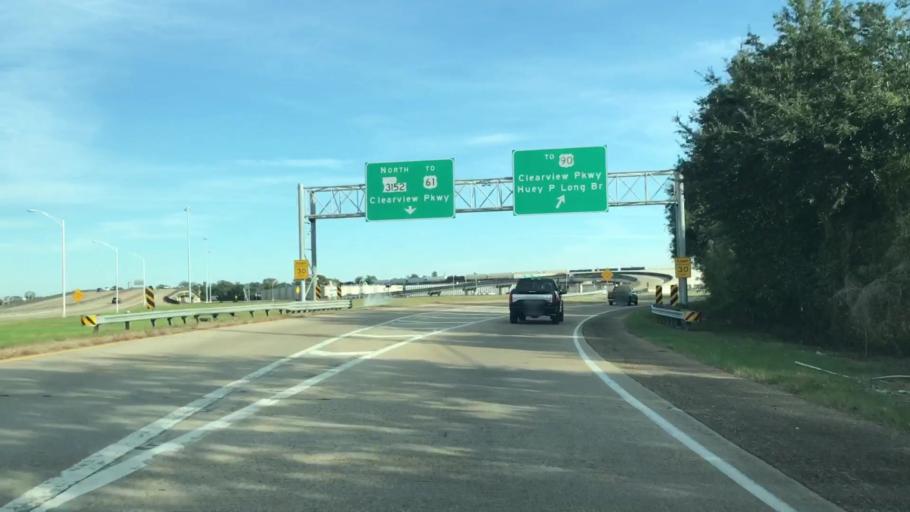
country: US
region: Louisiana
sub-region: Jefferson Parish
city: Elmwood
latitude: 29.9682
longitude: -90.1877
